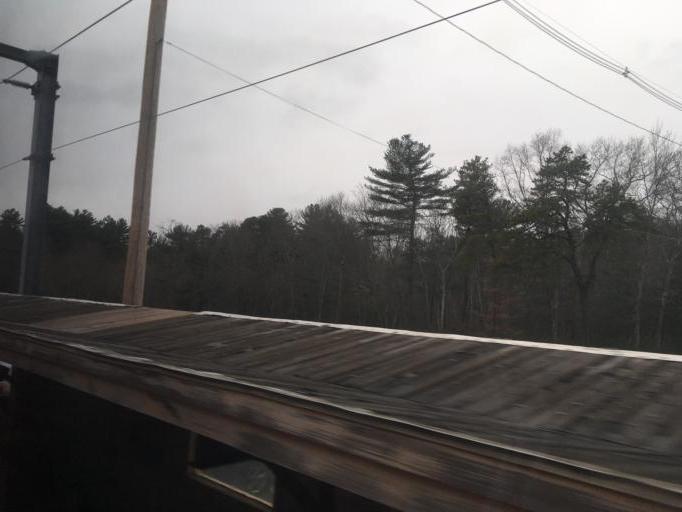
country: US
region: Massachusetts
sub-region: Norfolk County
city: Sharon
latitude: 42.1247
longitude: -71.1843
